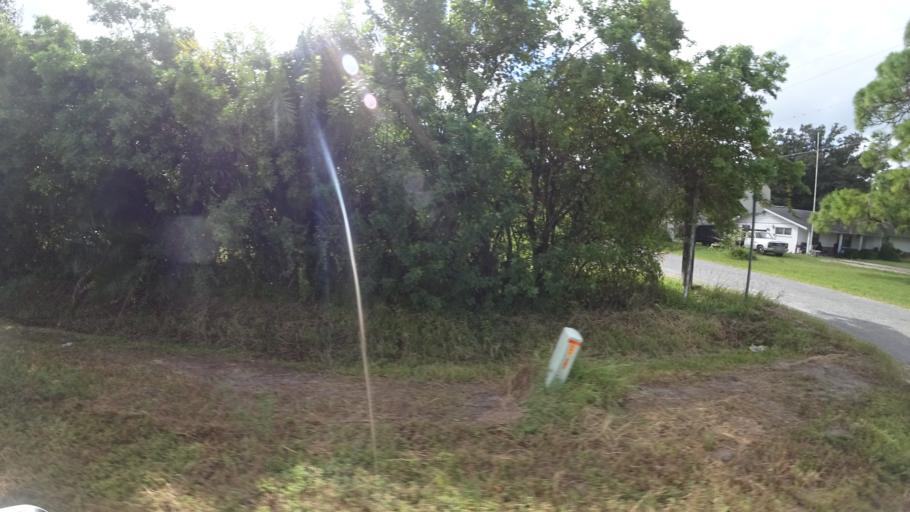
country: US
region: Florida
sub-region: Manatee County
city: Samoset
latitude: 27.4767
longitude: -82.5097
